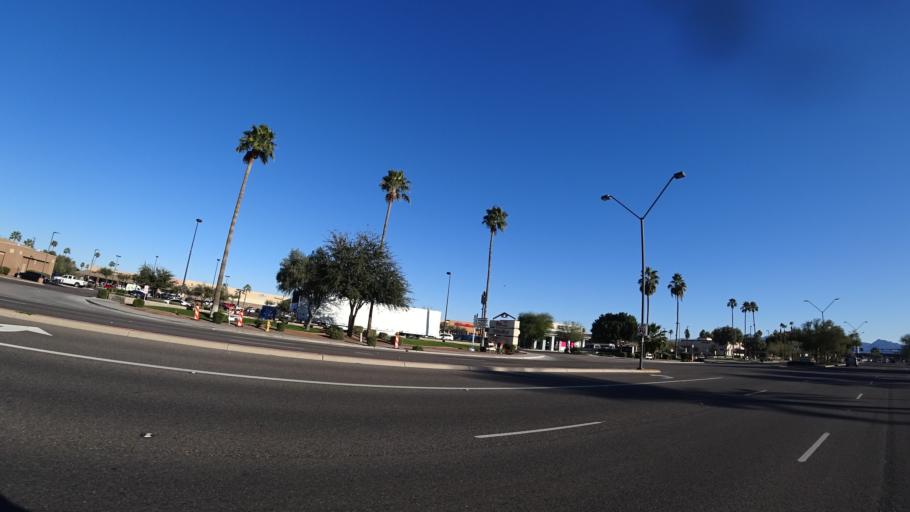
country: US
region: Arizona
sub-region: Maricopa County
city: Avondale
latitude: 33.4634
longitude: -112.3411
